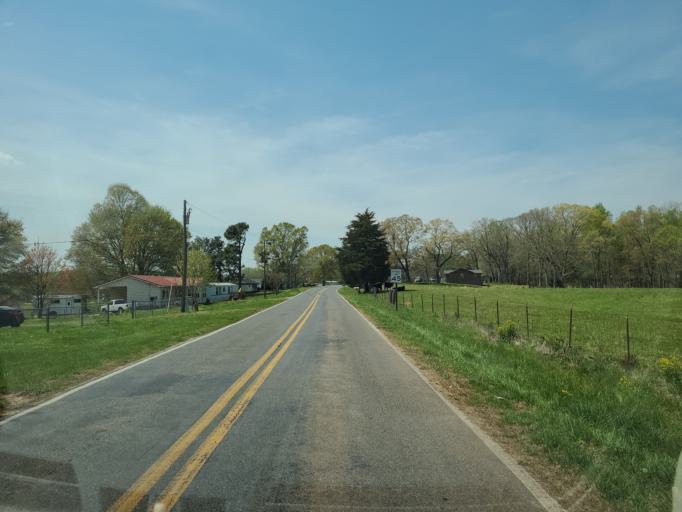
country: US
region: North Carolina
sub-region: Cleveland County
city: Shelby
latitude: 35.2563
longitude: -81.4835
